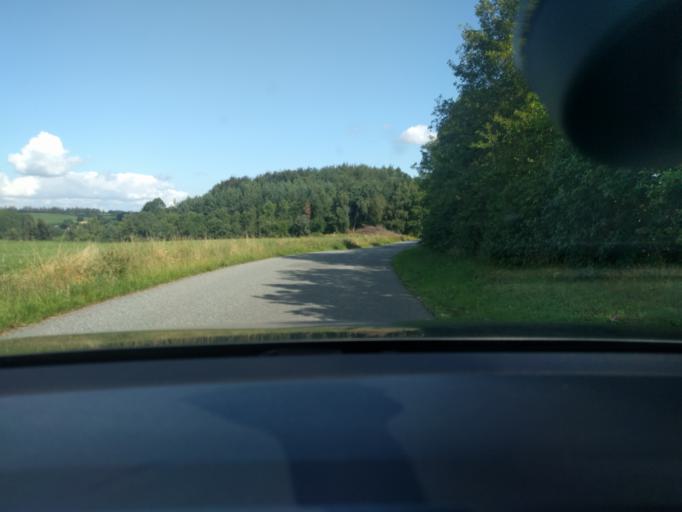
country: DK
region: Central Jutland
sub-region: Viborg Kommune
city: Viborg
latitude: 56.5078
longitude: 9.3048
